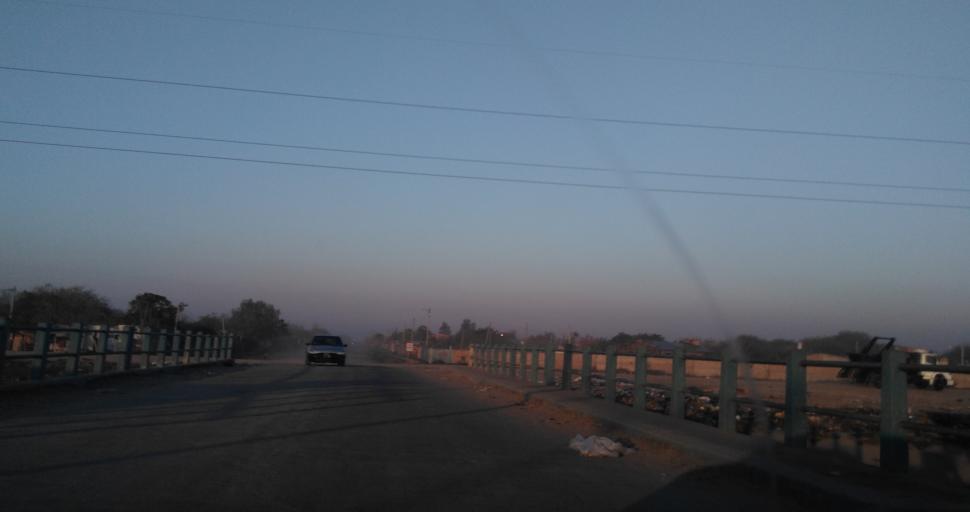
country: AR
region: Chaco
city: Resistencia
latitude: -27.4832
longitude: -58.9939
